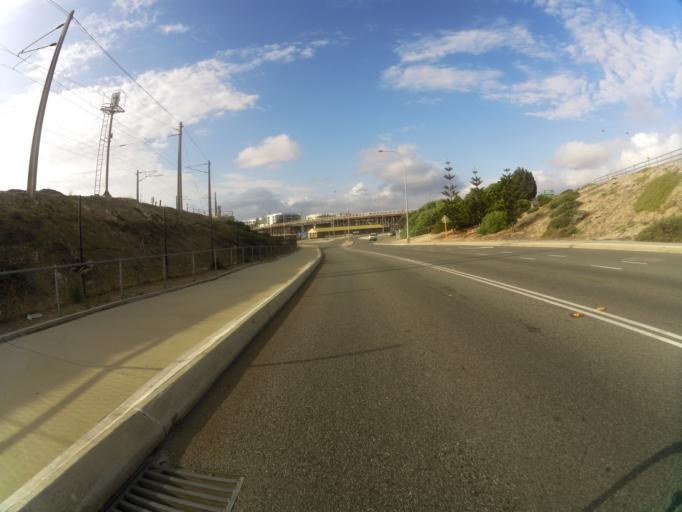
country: AU
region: Western Australia
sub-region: Fremantle
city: North Fremantle
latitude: -32.0433
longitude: 115.7536
